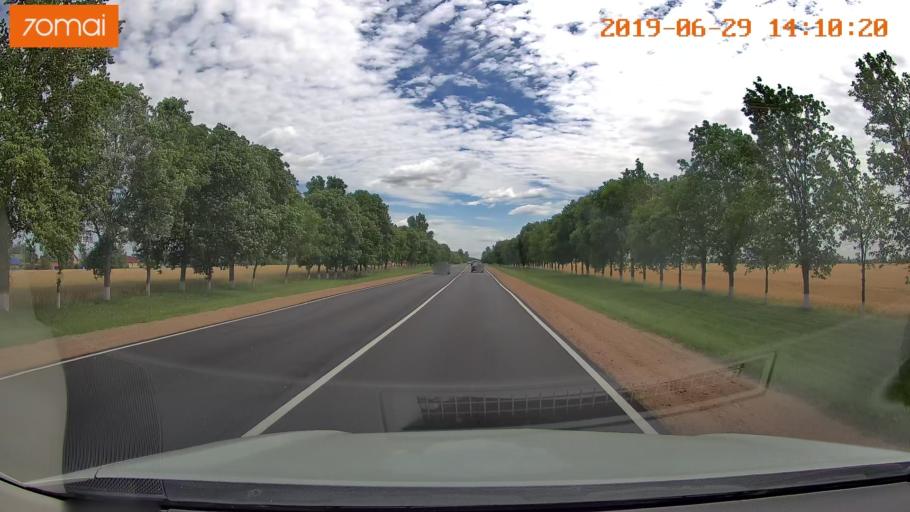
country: BY
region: Minsk
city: Salihorsk
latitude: 52.8309
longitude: 27.4933
